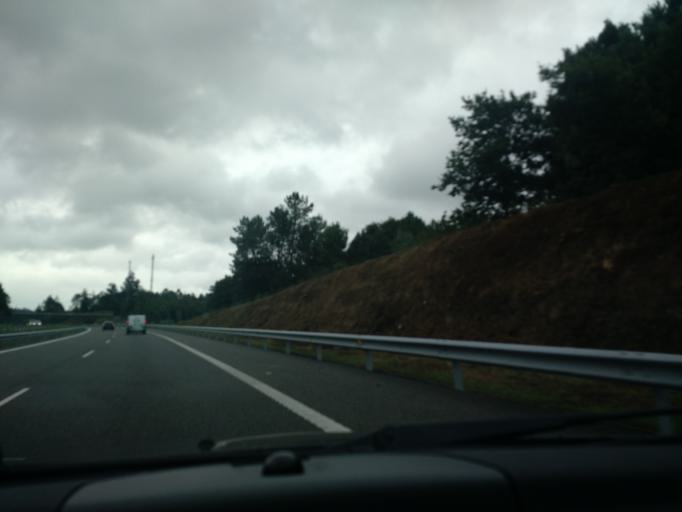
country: ES
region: Galicia
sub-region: Provincia da Coruna
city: Ordes
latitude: 43.0479
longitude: -8.3768
